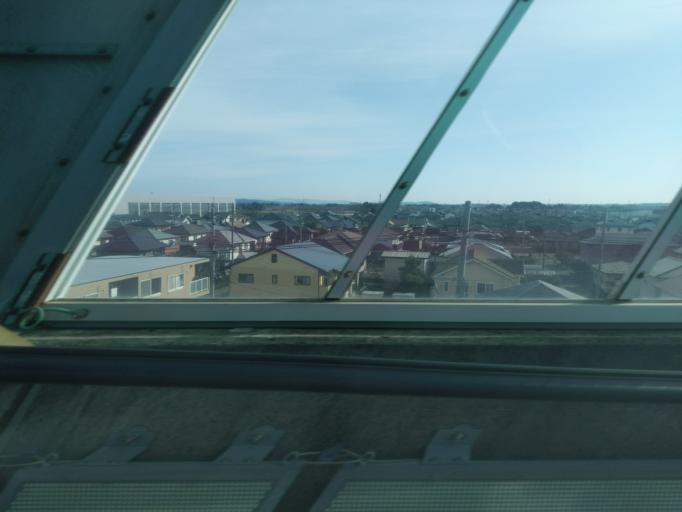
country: JP
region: Miyagi
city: Furukawa
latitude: 38.5838
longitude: 140.9717
